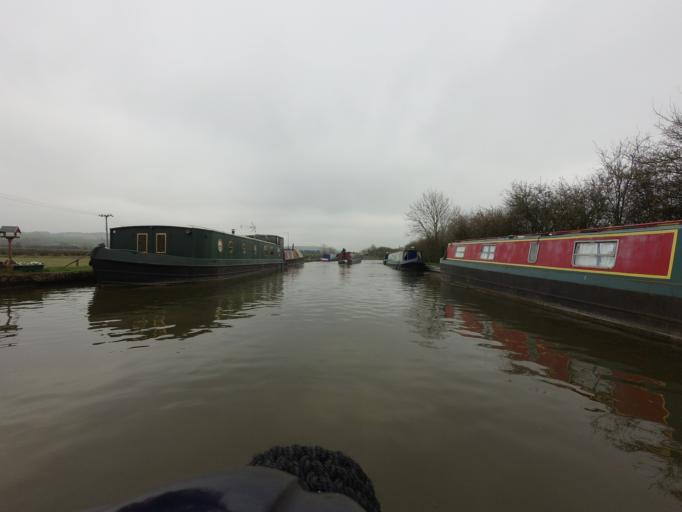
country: GB
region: England
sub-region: Buckinghamshire
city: Ivinghoe
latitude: 51.8477
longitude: -0.6444
